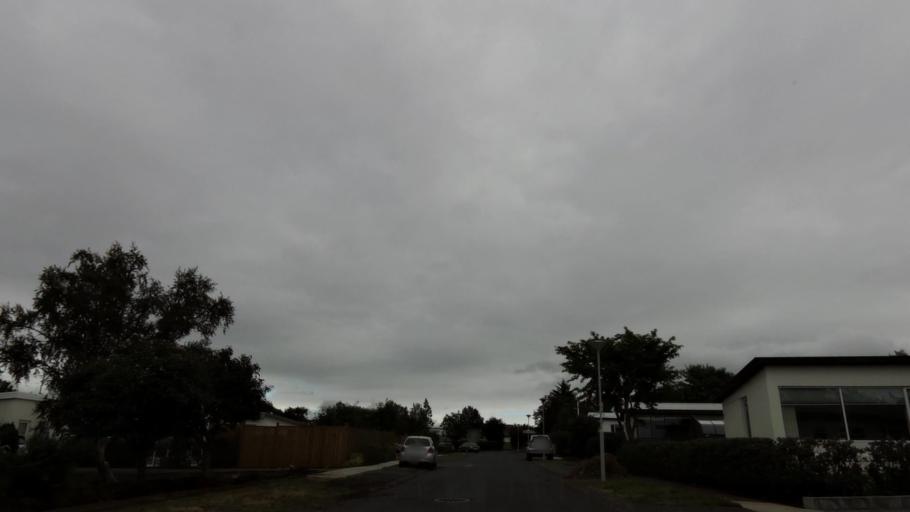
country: IS
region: Capital Region
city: Gardabaer
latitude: 64.0936
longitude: -21.9217
